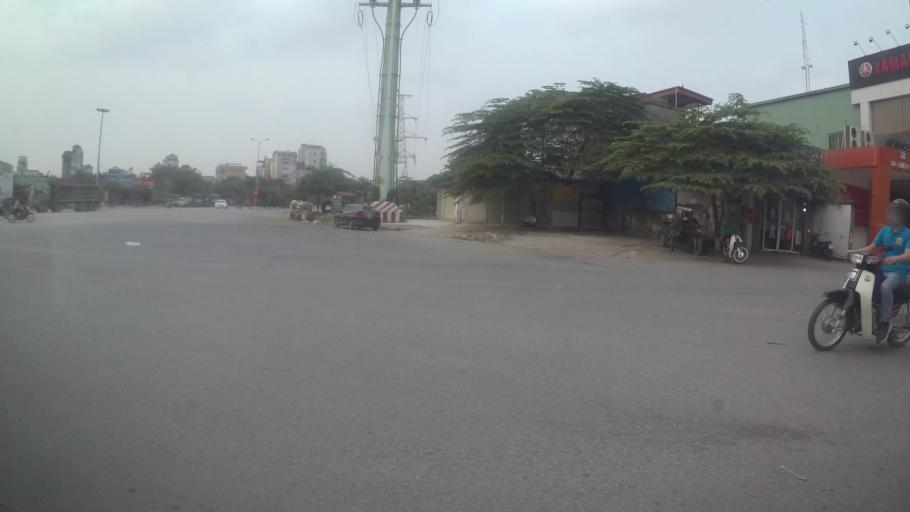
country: VN
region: Ha Noi
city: Cau Dien
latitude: 21.0466
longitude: 105.7486
